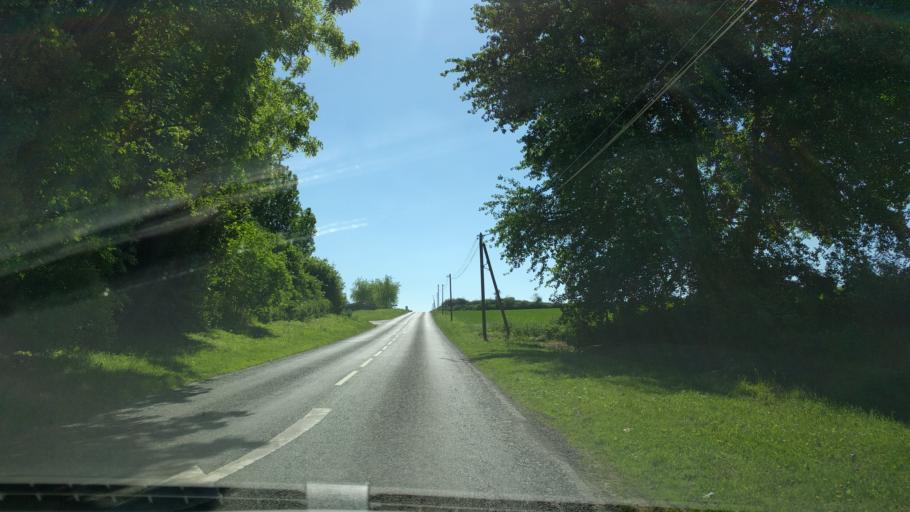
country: FR
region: Picardie
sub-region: Departement de la Somme
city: Peronne
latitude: 49.9143
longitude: 2.9247
